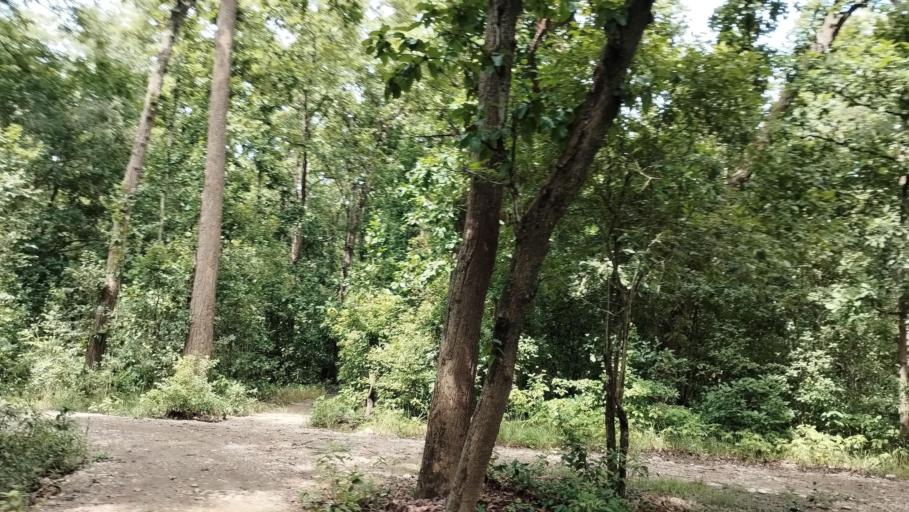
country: NP
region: Far Western
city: Tikapur
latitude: 28.4798
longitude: 81.2549
